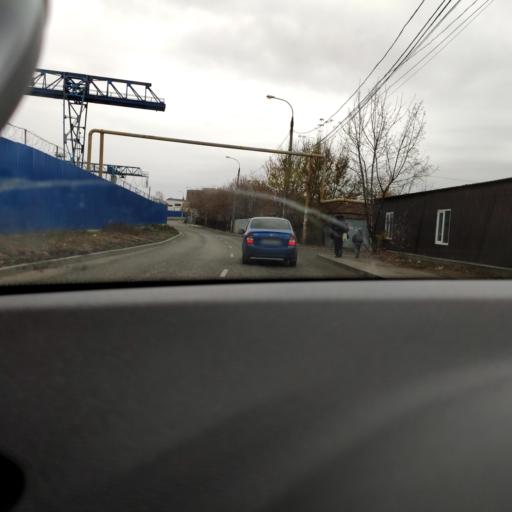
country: RU
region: Samara
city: Samara
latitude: 53.1799
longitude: 50.1368
